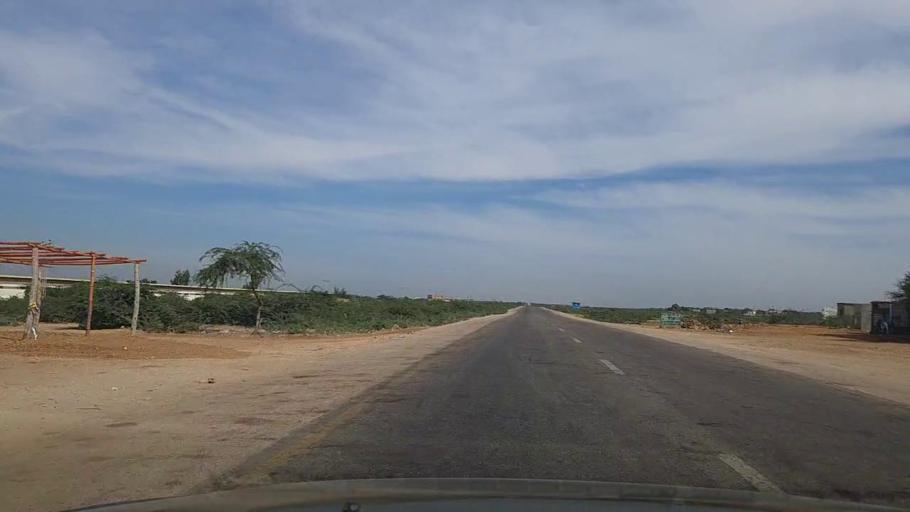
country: PK
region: Sindh
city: Thatta
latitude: 24.8365
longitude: 68.0013
